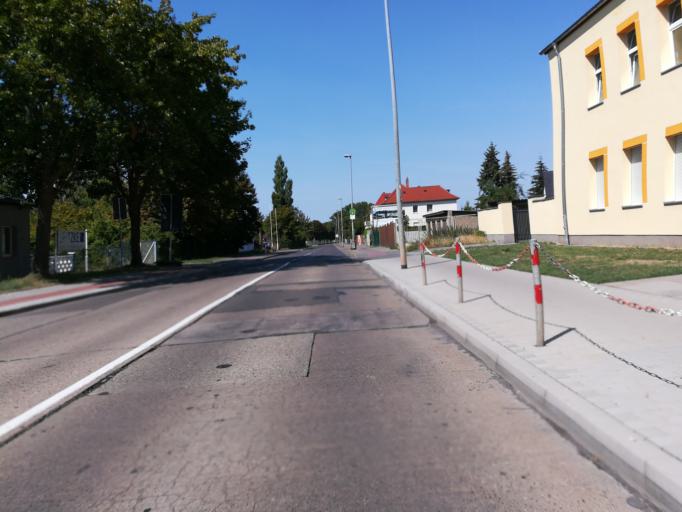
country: DE
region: Saxony-Anhalt
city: Magdeburg
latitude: 52.1404
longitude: 11.6130
